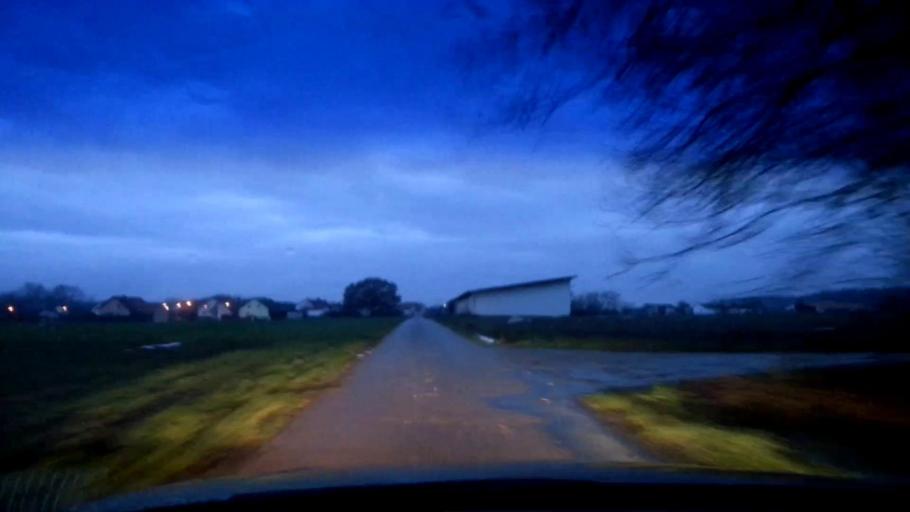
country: DE
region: Bavaria
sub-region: Upper Franconia
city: Memmelsdorf
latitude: 49.9624
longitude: 10.9608
